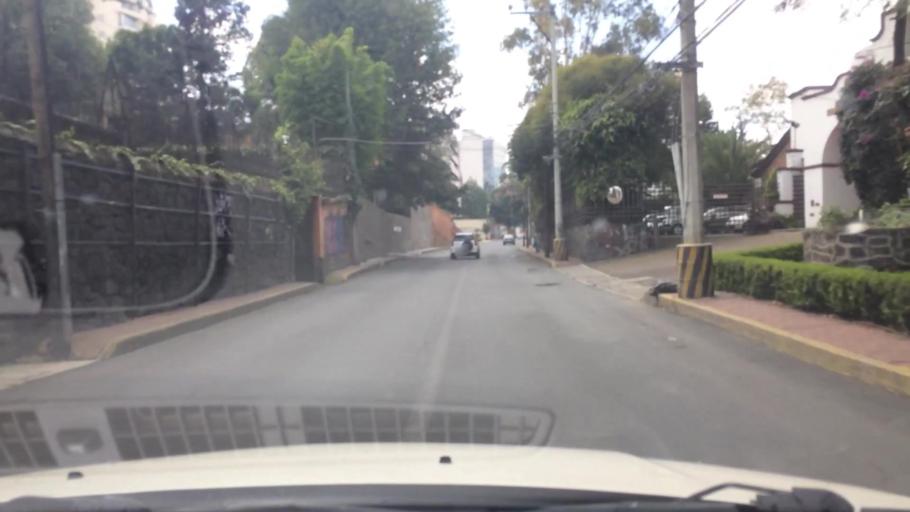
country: MX
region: Mexico City
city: Magdalena Contreras
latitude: 19.3257
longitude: -99.2171
